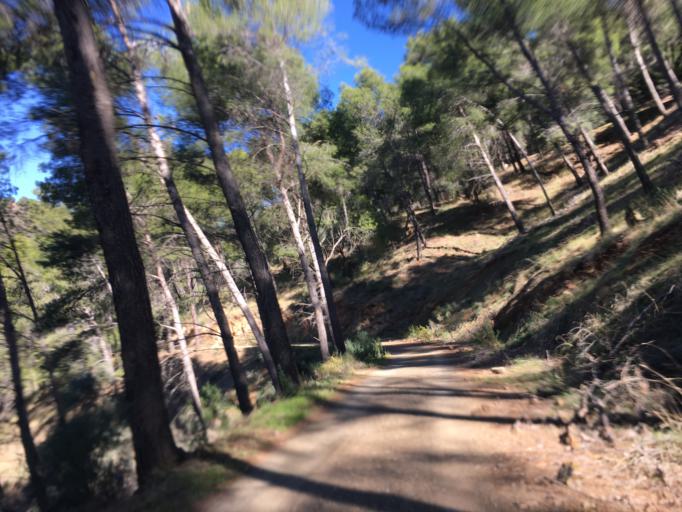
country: ES
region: Andalusia
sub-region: Provincia de Malaga
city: Malaga
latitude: 36.8006
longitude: -4.3993
